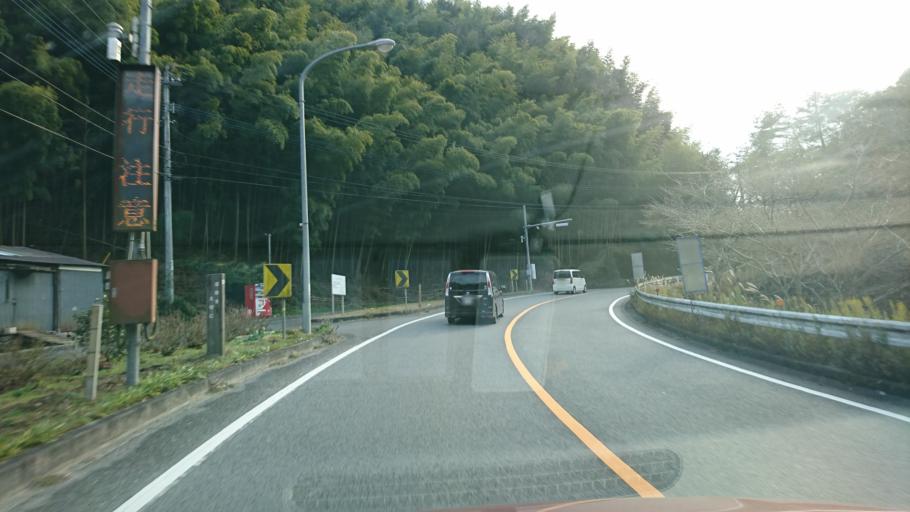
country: JP
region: Ehime
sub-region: Shikoku-chuo Shi
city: Matsuyama
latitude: 33.8948
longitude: 132.8439
